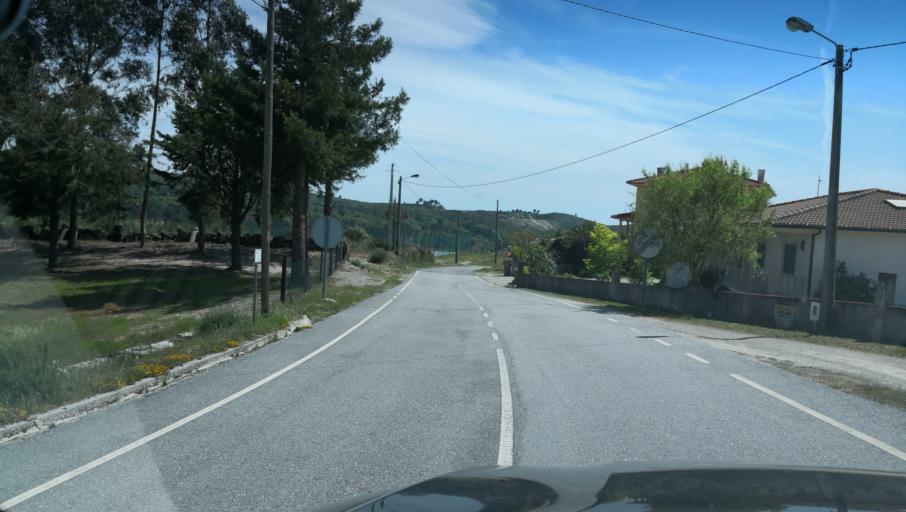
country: PT
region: Vila Real
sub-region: Vila Real
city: Vila Real
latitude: 41.3611
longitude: -7.6981
